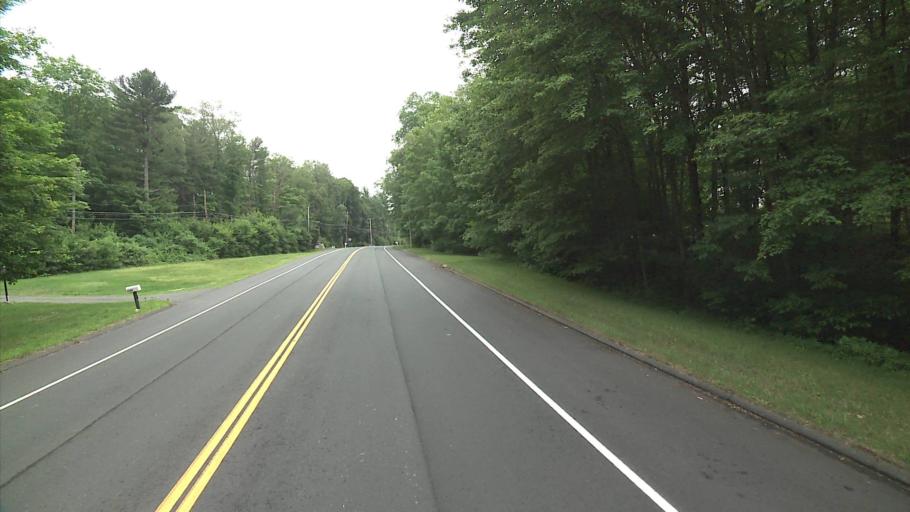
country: US
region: Connecticut
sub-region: Hartford County
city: Manchester
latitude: 41.7111
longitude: -72.5216
